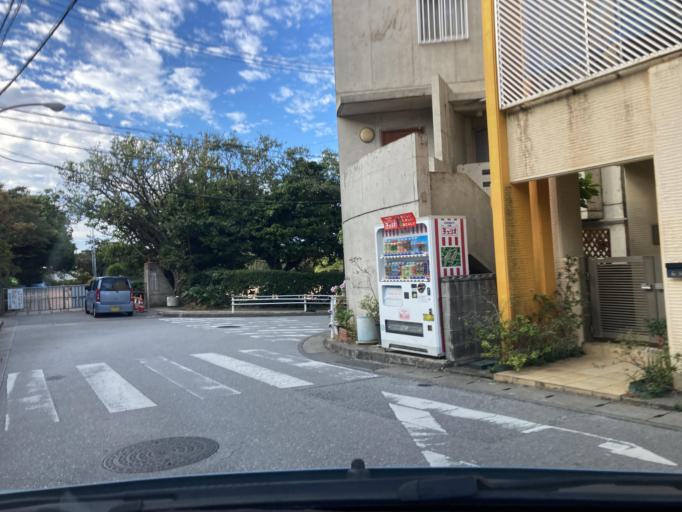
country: JP
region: Okinawa
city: Naha-shi
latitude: 26.2280
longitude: 127.7220
